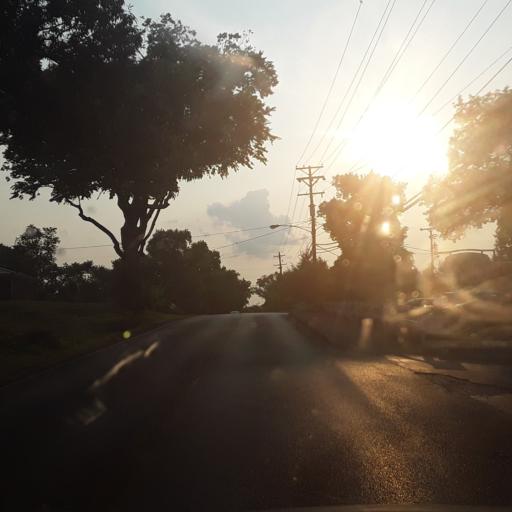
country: US
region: Tennessee
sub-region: Williamson County
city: Brentwood
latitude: 36.0549
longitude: -86.7287
